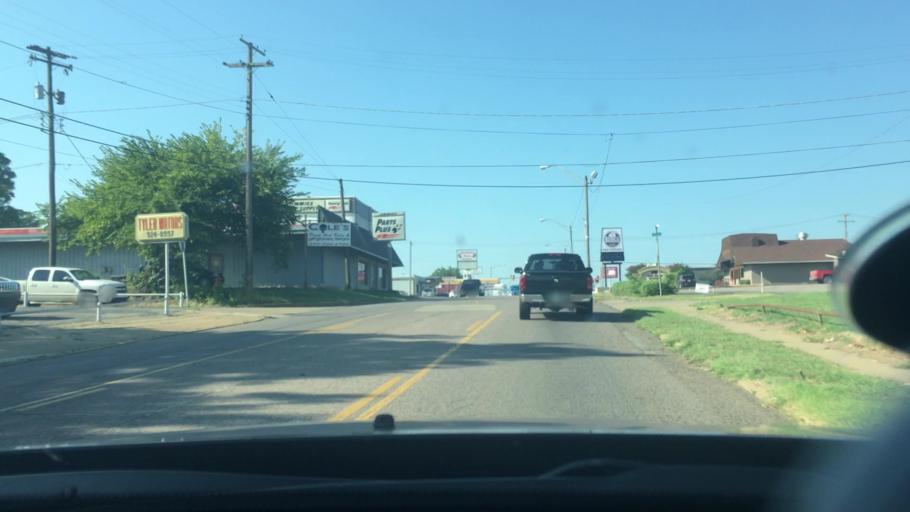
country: US
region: Oklahoma
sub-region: Bryan County
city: Durant
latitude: 33.9999
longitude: -96.3732
